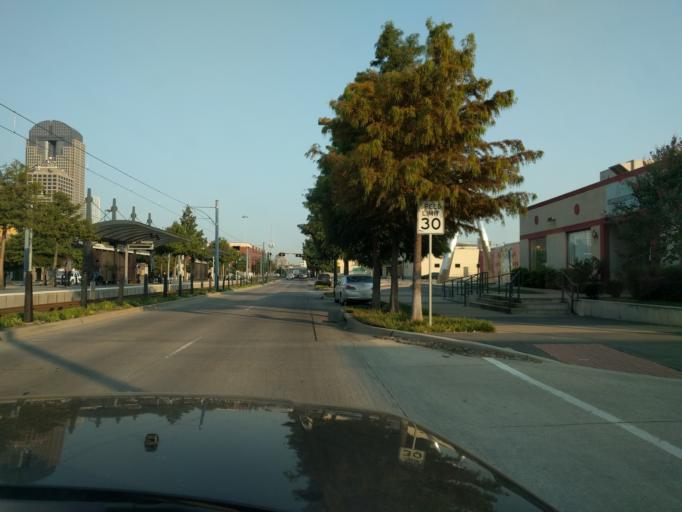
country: US
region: Texas
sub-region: Dallas County
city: Dallas
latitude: 32.7857
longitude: -96.7881
